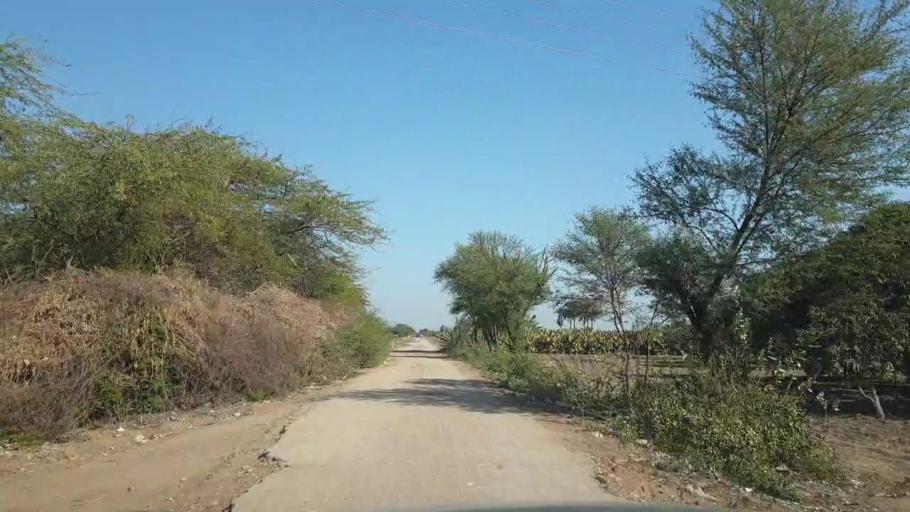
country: PK
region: Sindh
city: Tando Adam
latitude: 25.6625
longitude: 68.6895
